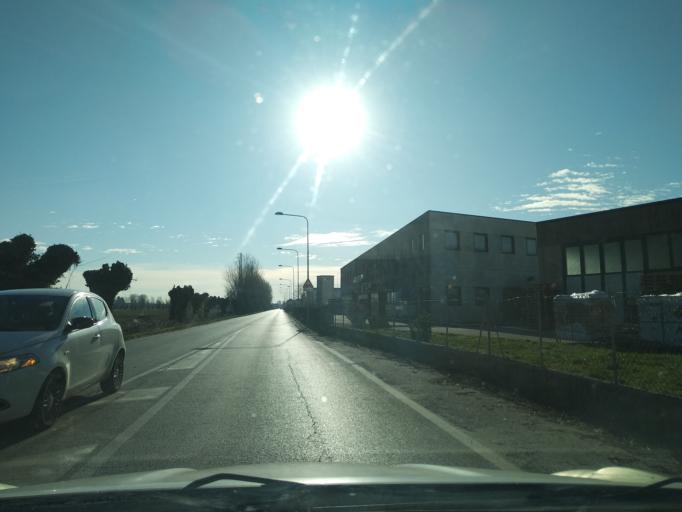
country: IT
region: Veneto
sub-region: Provincia di Vicenza
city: Quinto Vicentino
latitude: 45.5879
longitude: 11.6457
